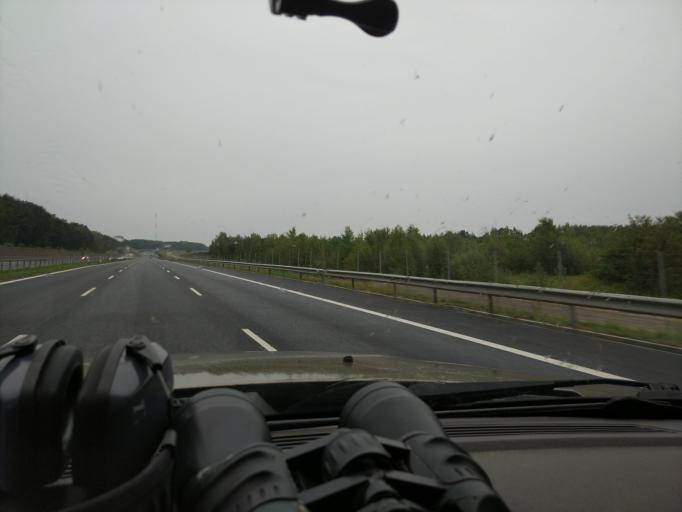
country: PL
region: Masovian Voivodeship
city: Zielonka
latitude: 52.3374
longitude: 21.1568
